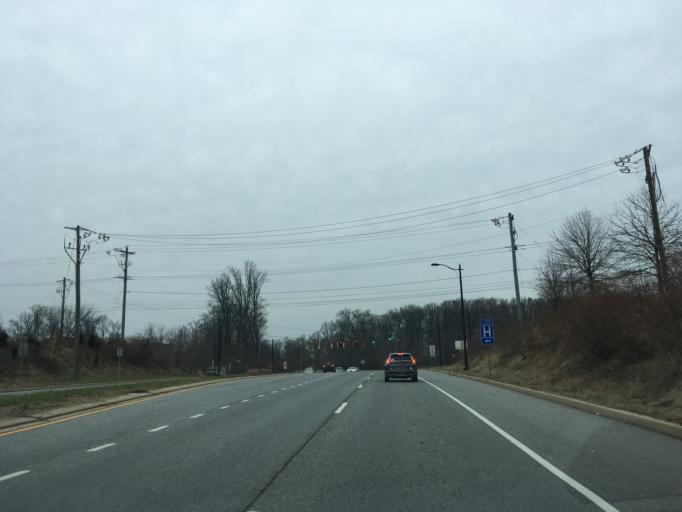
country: US
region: Delaware
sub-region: New Castle County
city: Wilmington
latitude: 39.7826
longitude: -75.5523
